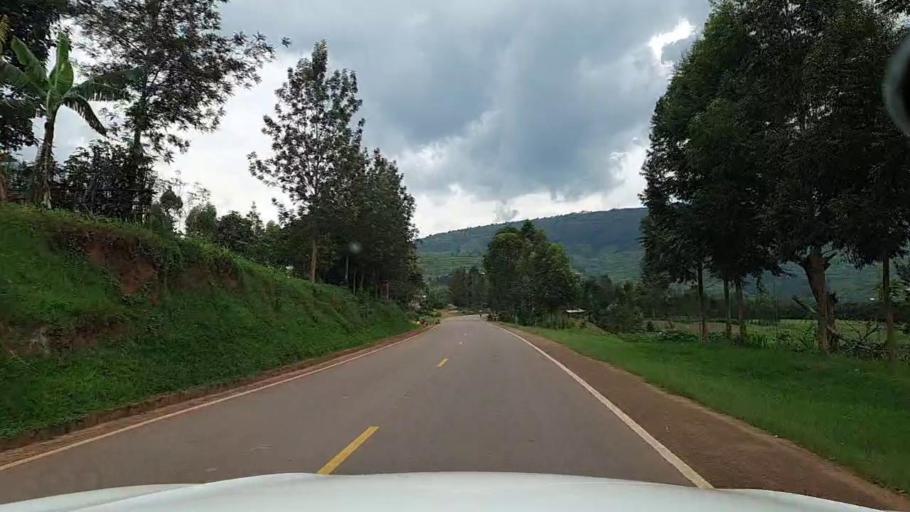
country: RW
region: Kigali
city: Kigali
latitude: -1.7850
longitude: 30.1295
